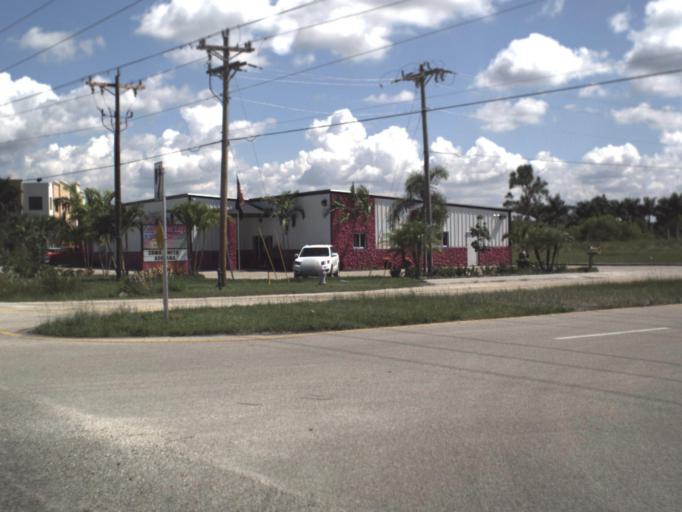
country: US
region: Florida
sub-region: Lee County
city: Lochmoor Waterway Estates
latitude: 26.6490
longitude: -81.9816
